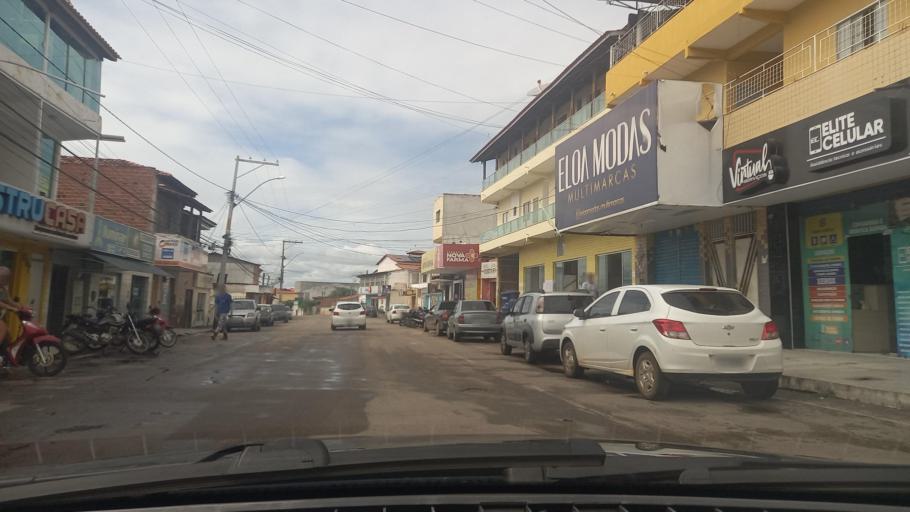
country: BR
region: Bahia
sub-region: Paulo Afonso
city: Paulo Afonso
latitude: -9.4434
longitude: -38.2160
